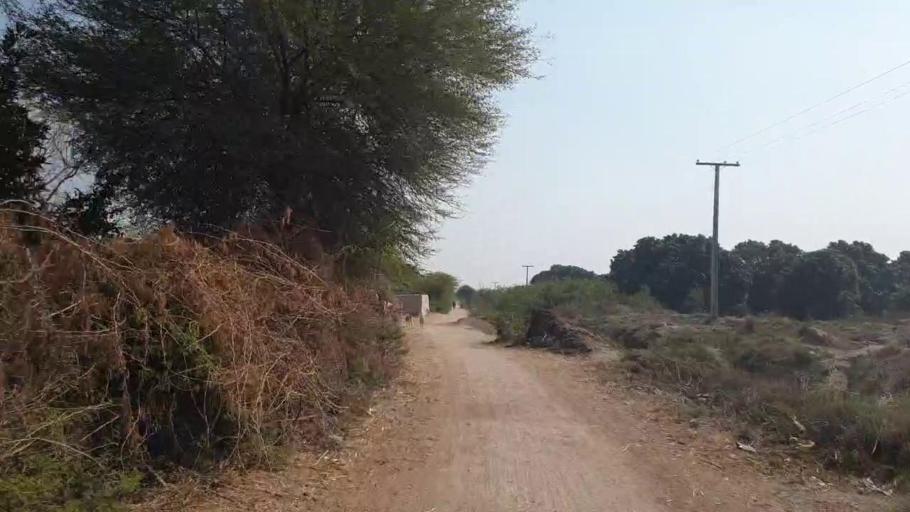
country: PK
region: Sindh
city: Chambar
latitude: 25.4114
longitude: 68.8983
